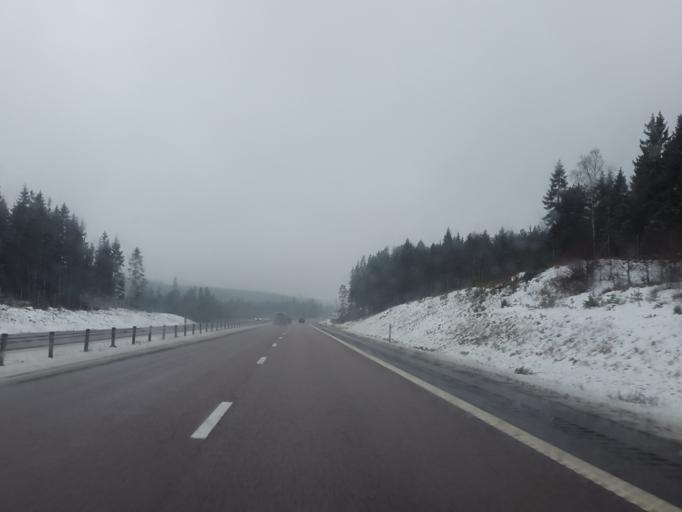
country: SE
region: Vaestra Goetaland
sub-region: Boras Kommun
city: Dalsjofors
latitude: 57.7484
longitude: 13.0703
